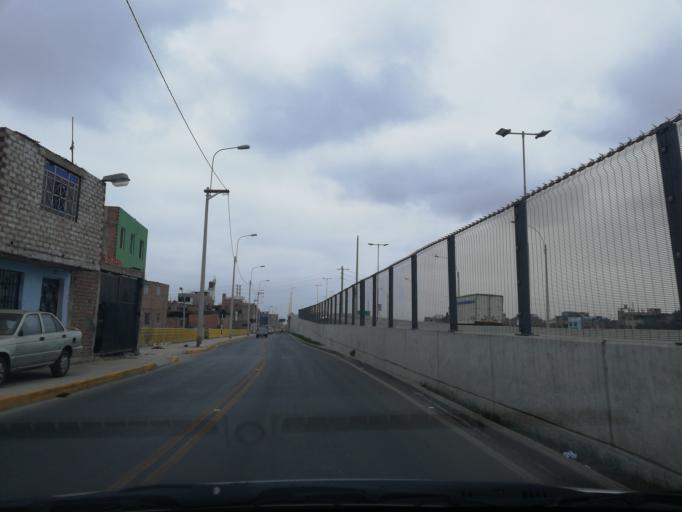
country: PE
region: Lima
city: Lima
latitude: -12.0357
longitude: -77.0633
